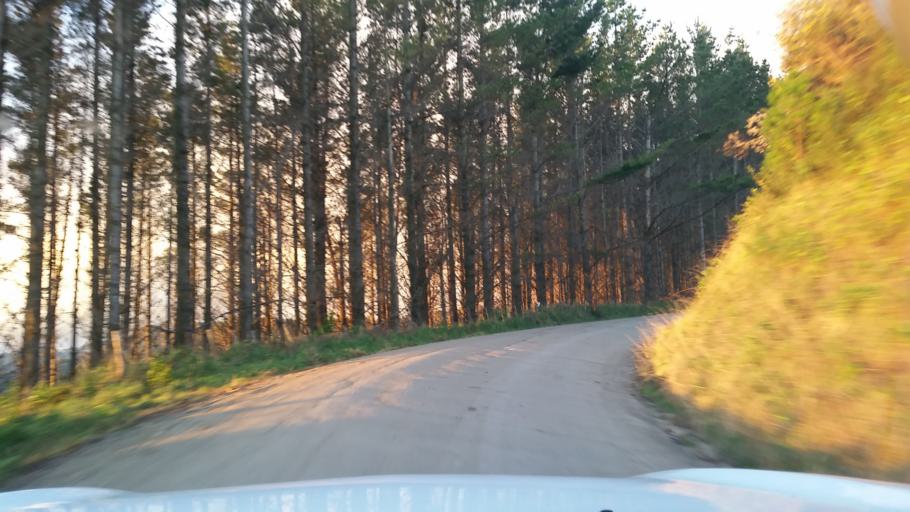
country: NZ
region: Manawatu-Wanganui
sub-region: Wanganui District
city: Wanganui
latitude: -39.7736
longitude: 174.8623
